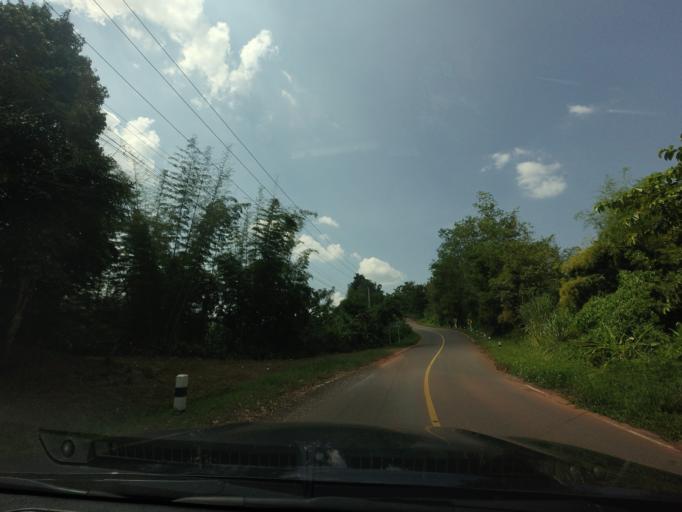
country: TH
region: Nan
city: Bo Kluea
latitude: 19.0112
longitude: 101.1988
